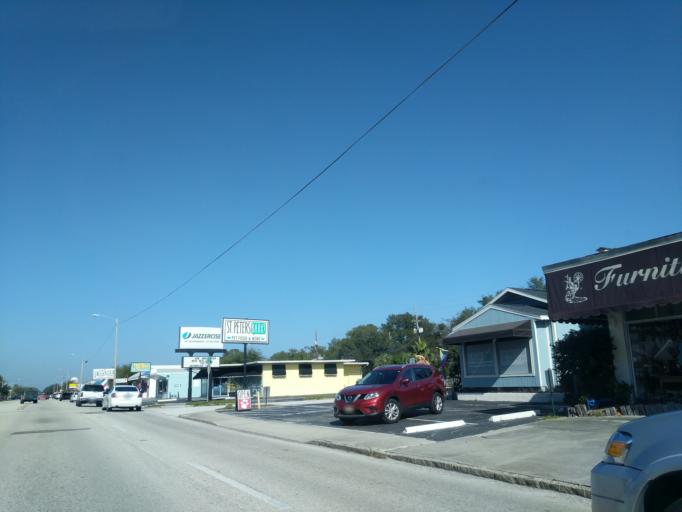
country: US
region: Florida
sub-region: Pinellas County
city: Saint Petersburg
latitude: 27.7944
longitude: -82.6467
